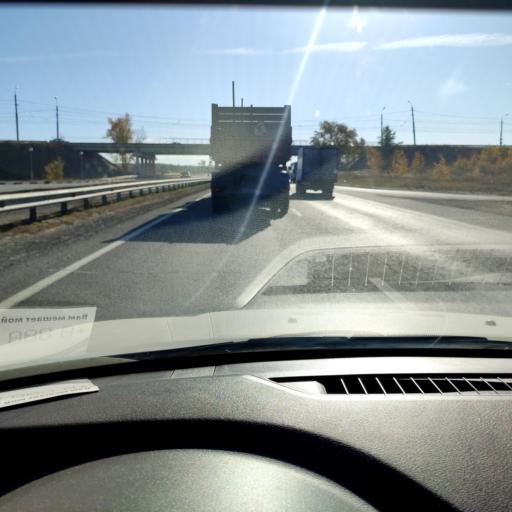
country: RU
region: Samara
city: Zhigulevsk
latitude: 53.5185
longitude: 49.5334
